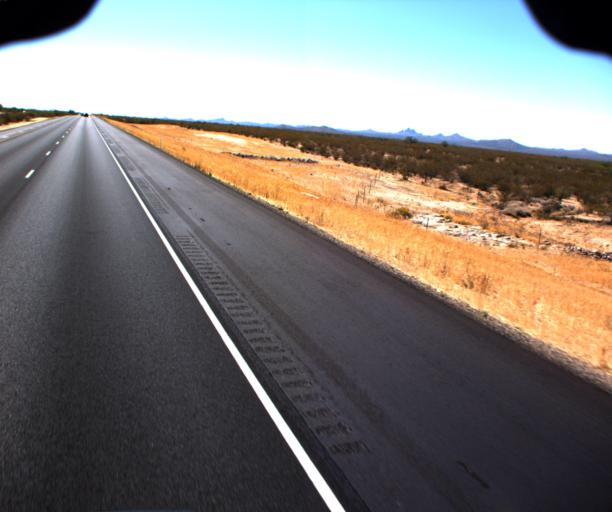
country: US
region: Arizona
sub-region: Yavapai County
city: Congress
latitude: 34.0784
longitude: -112.8865
